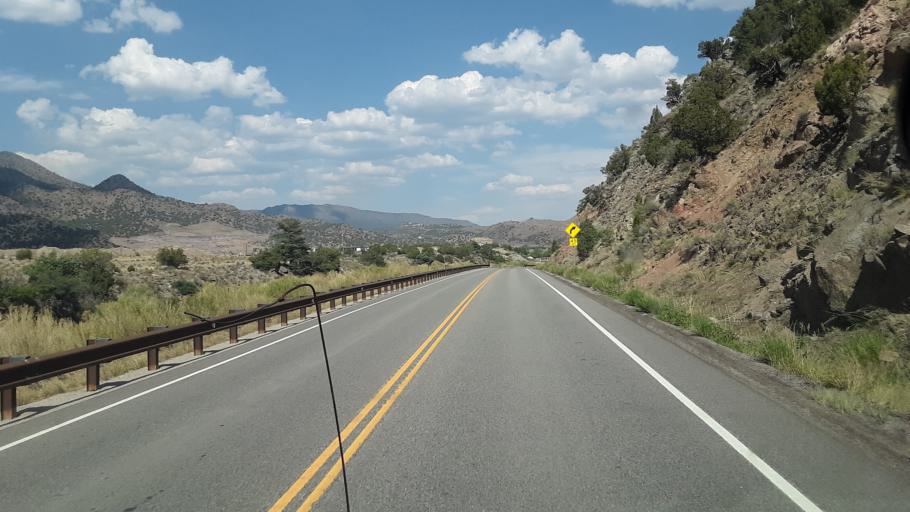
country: US
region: Colorado
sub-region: Fremont County
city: Canon City
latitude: 38.4852
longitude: -105.4049
